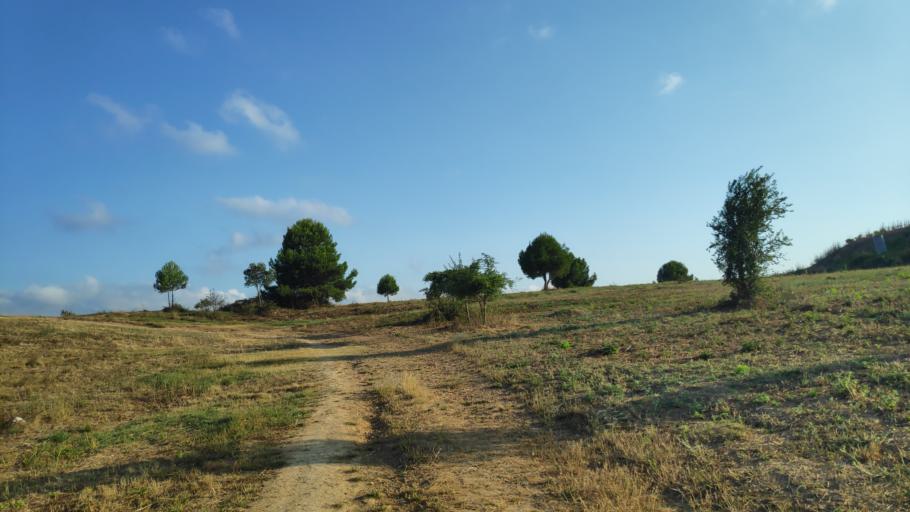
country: ES
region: Catalonia
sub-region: Provincia de Barcelona
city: Cerdanyola del Valles
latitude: 41.4918
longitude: 2.1189
